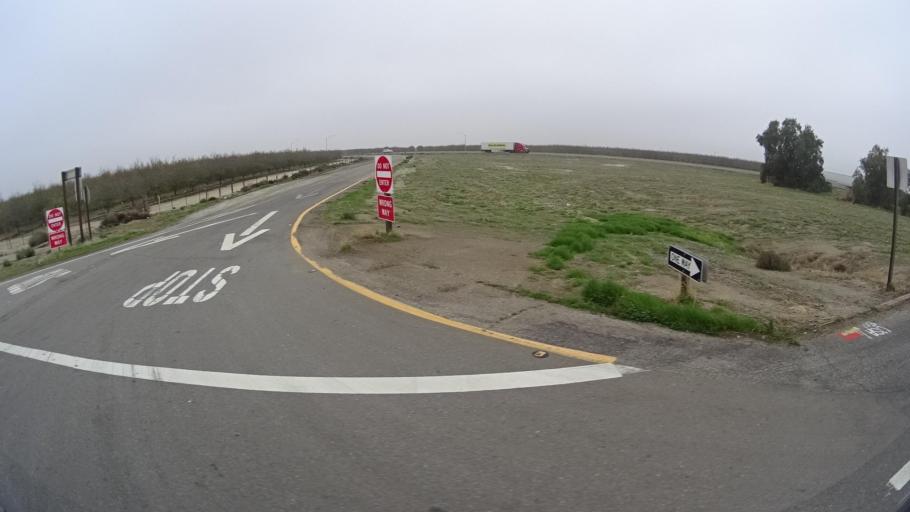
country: US
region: California
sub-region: Kern County
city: Greenfield
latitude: 35.2091
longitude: -119.1607
